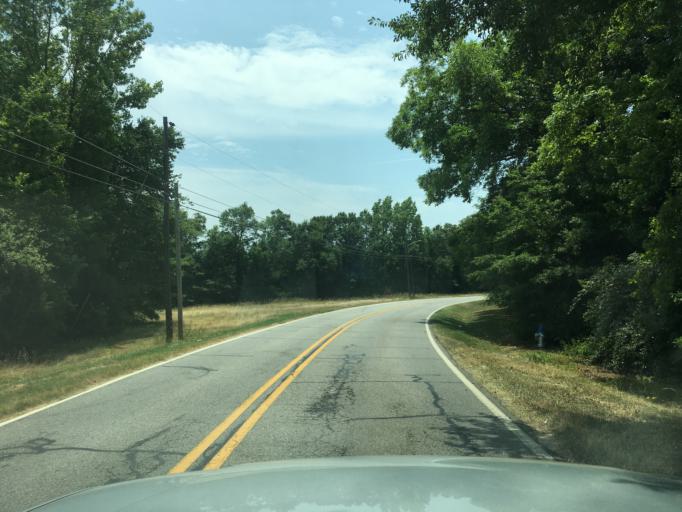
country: US
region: Georgia
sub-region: Hart County
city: Hartwell
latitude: 34.3447
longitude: -82.9192
